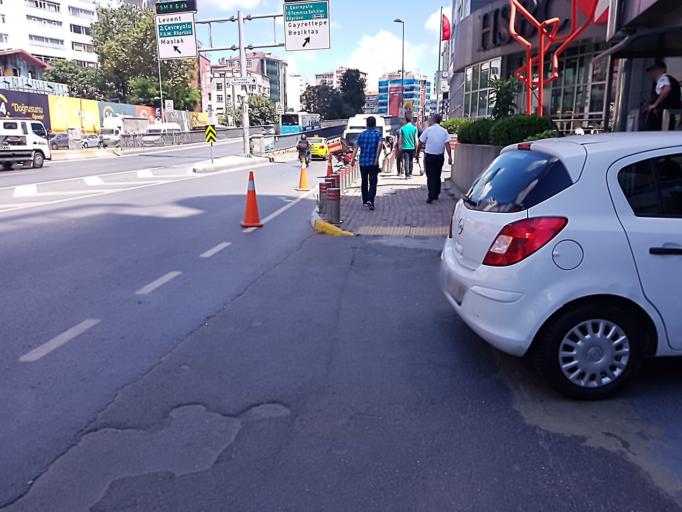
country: TR
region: Istanbul
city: Sisli
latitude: 41.0695
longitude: 29.0127
